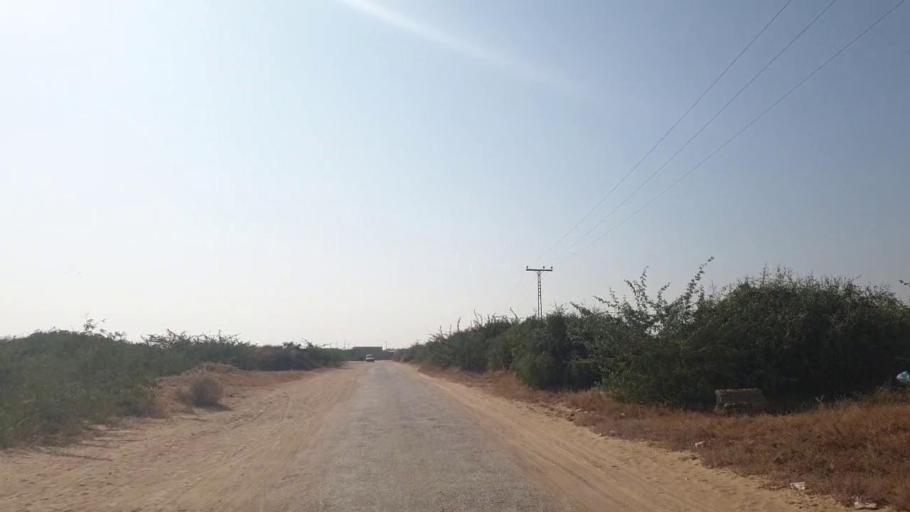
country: PK
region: Sindh
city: Thatta
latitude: 25.1364
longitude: 67.7720
